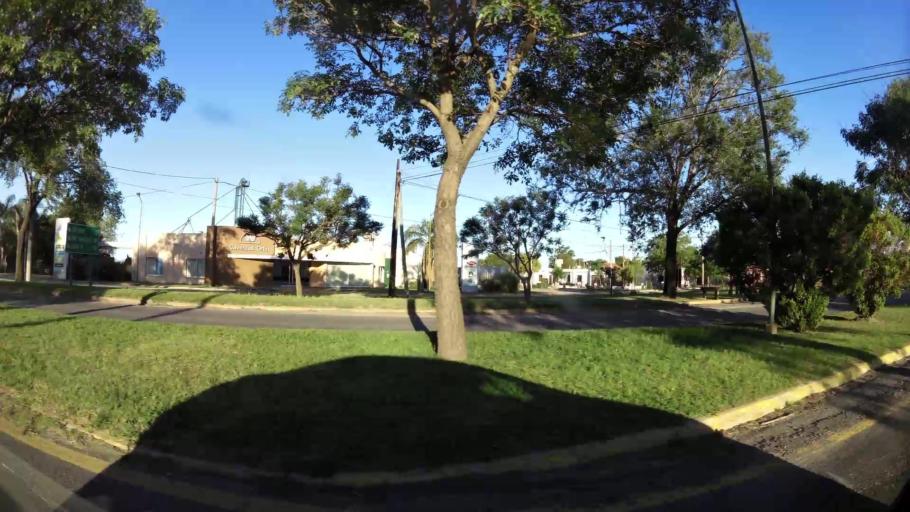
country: AR
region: Cordoba
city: Las Varillas
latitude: -31.8684
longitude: -62.7076
